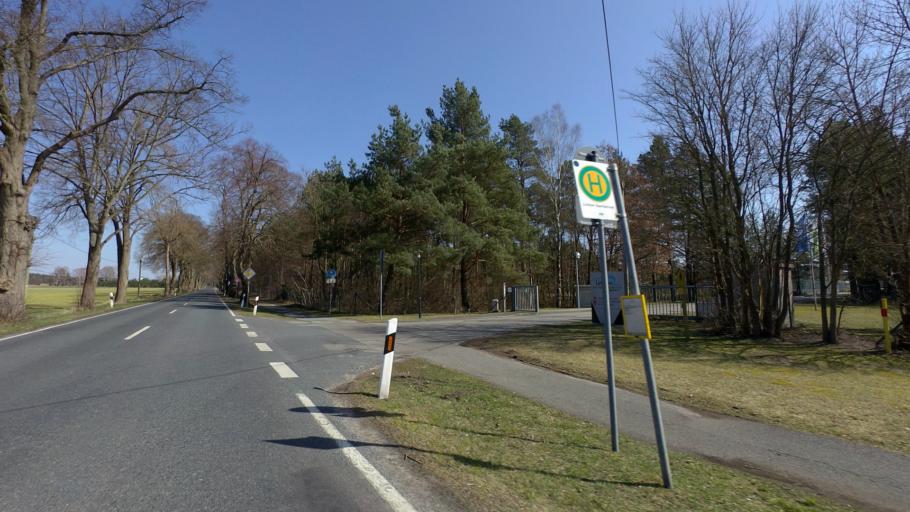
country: DE
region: Brandenburg
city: Lindow
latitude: 52.9787
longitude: 13.0063
